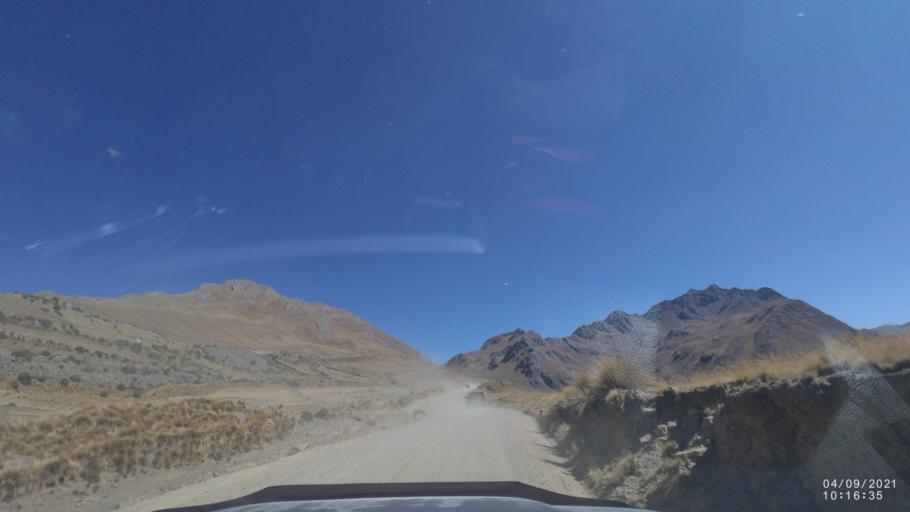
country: BO
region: Cochabamba
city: Sipe Sipe
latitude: -17.3213
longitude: -66.4191
